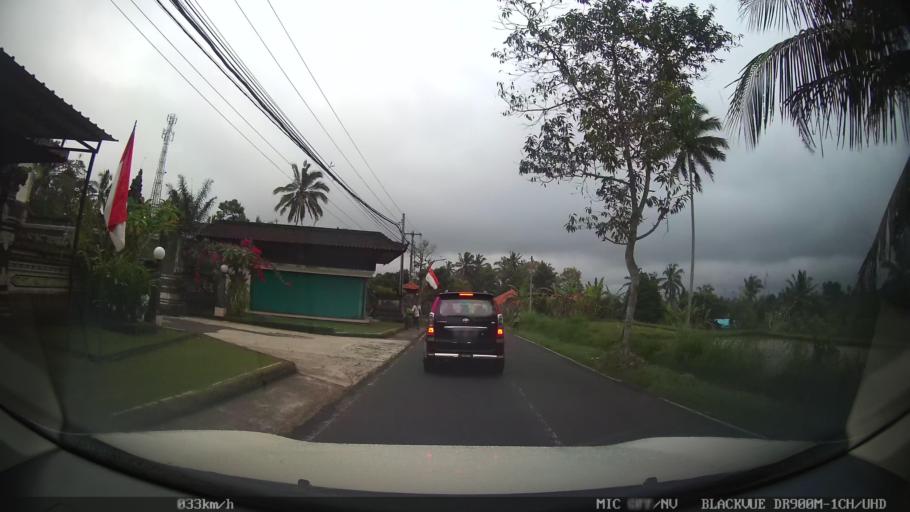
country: ID
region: Bali
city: Banjar Ponggang
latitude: -8.3953
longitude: 115.2525
